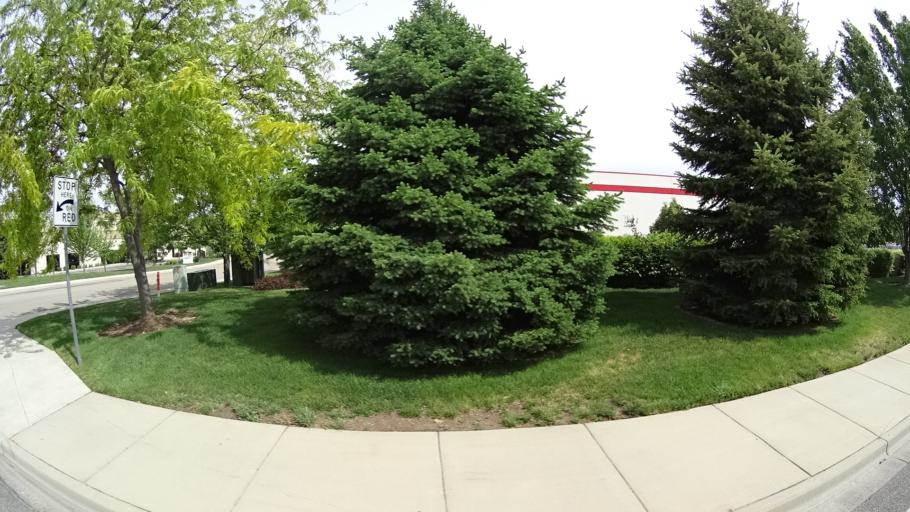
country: US
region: Idaho
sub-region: Ada County
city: Garden City
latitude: 43.5757
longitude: -116.2878
